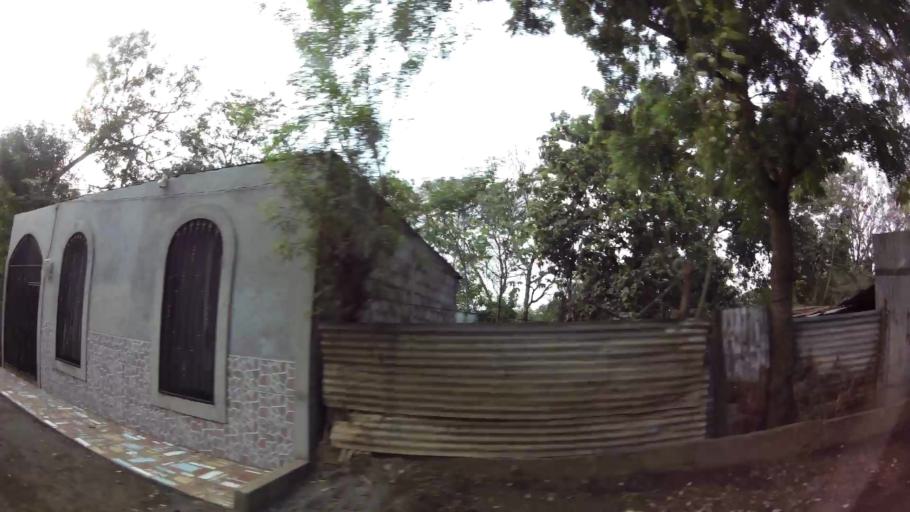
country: NI
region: Masaya
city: Masaya
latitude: 11.9872
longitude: -86.1060
